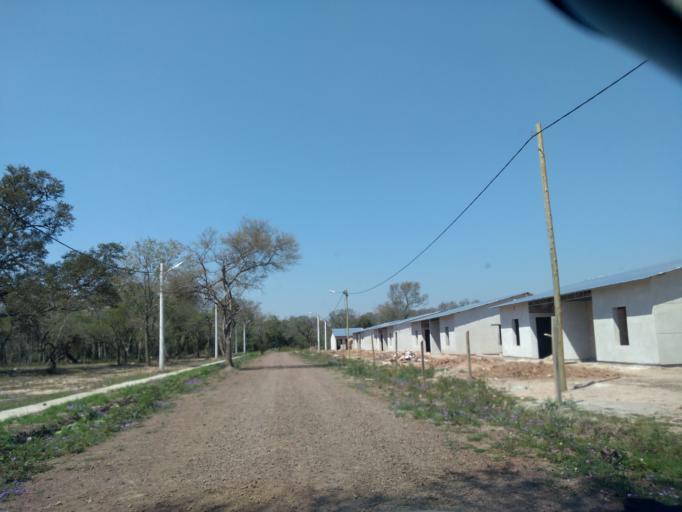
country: AR
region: Chaco
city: Resistencia
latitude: -27.4122
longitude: -58.9563
